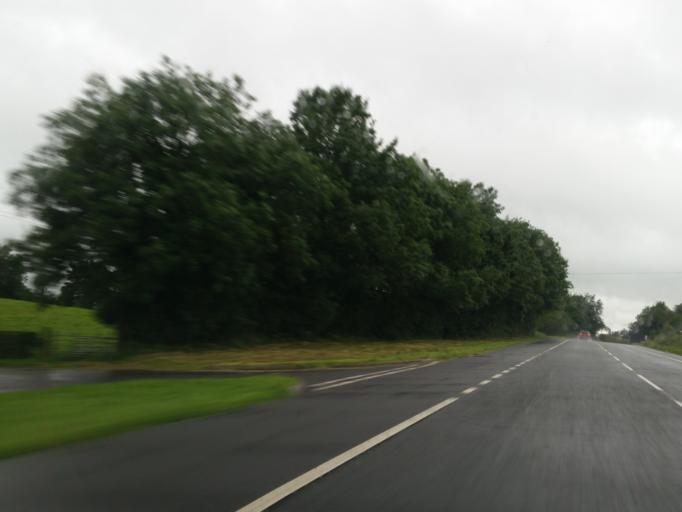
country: GB
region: Northern Ireland
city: Fivemiletown
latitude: 54.3691
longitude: -7.3357
